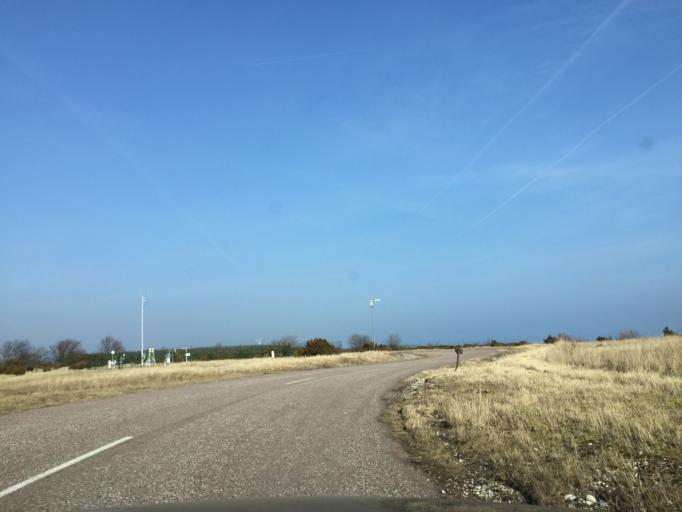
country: LV
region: Dundaga
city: Dundaga
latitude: 57.9129
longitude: 22.0573
